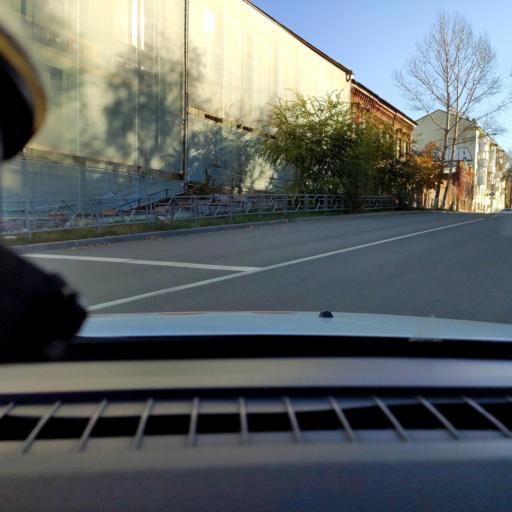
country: RU
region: Samara
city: Rozhdestveno
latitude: 53.1819
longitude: 50.0804
